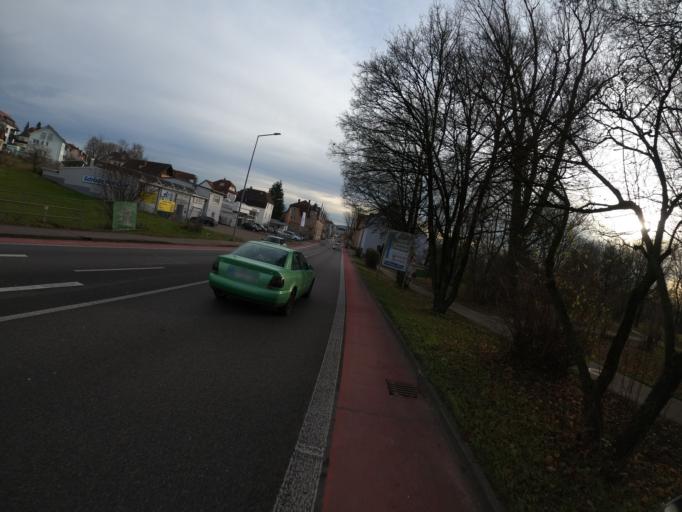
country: DE
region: Baden-Wuerttemberg
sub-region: Regierungsbezirk Stuttgart
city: Goeppingen
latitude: 48.7132
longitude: 9.6474
